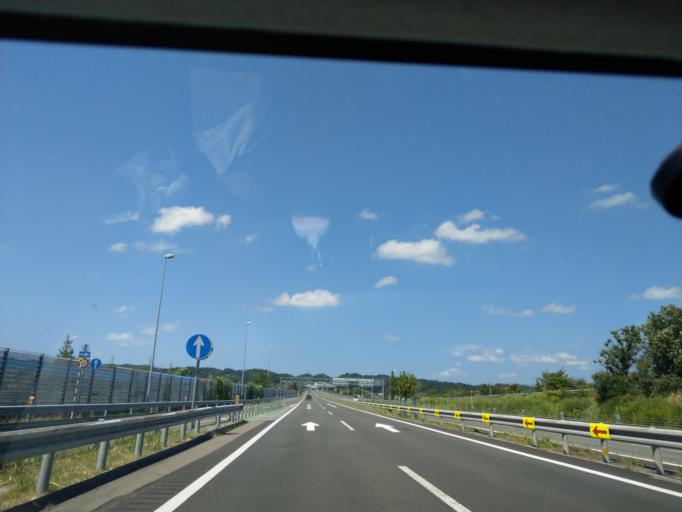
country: JP
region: Akita
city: Akita
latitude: 39.6426
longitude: 140.2100
